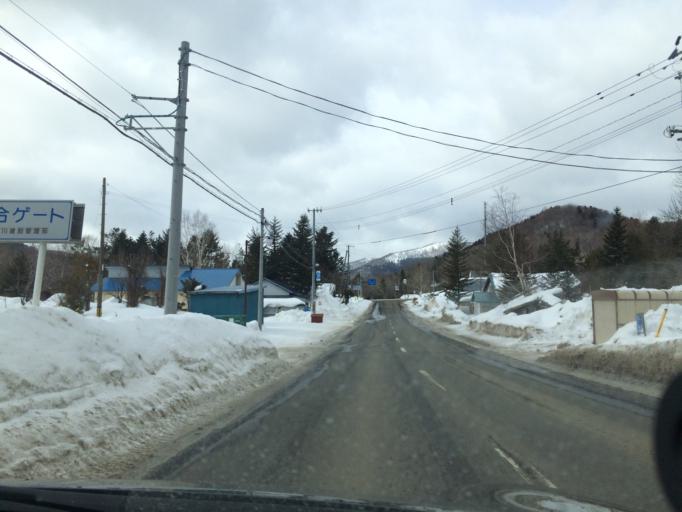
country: JP
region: Hokkaido
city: Shimo-furano
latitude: 43.1232
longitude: 142.6787
